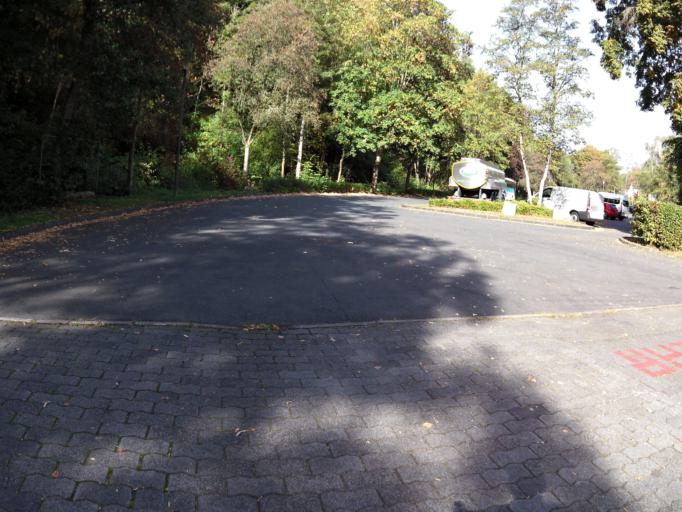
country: DE
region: Rheinland-Pfalz
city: Scheuern
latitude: 50.0075
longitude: 6.2965
